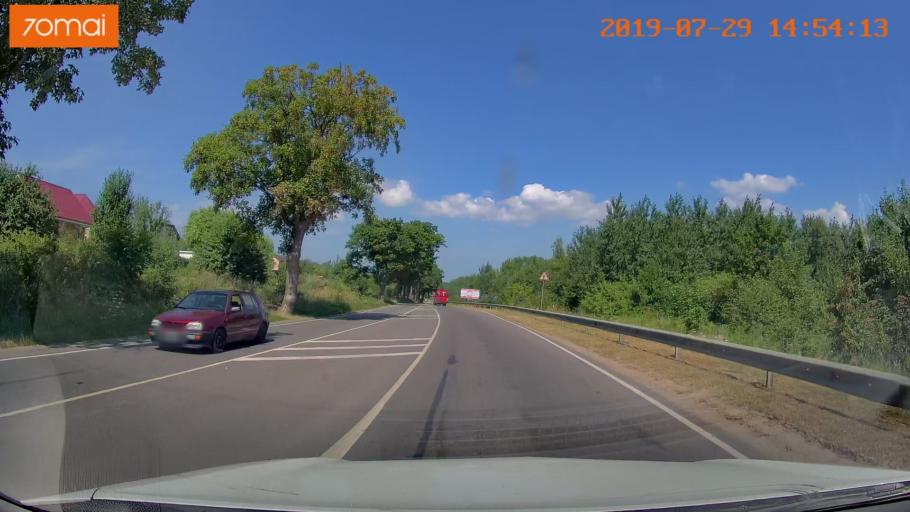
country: RU
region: Kaliningrad
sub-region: Gorod Kaliningrad
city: Baltiysk
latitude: 54.6722
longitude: 19.9233
